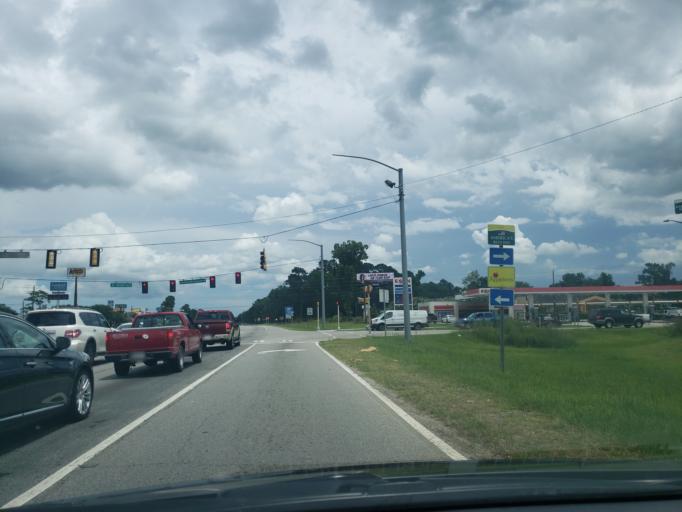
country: US
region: Georgia
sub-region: Chatham County
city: Georgetown
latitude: 32.0040
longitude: -81.2816
